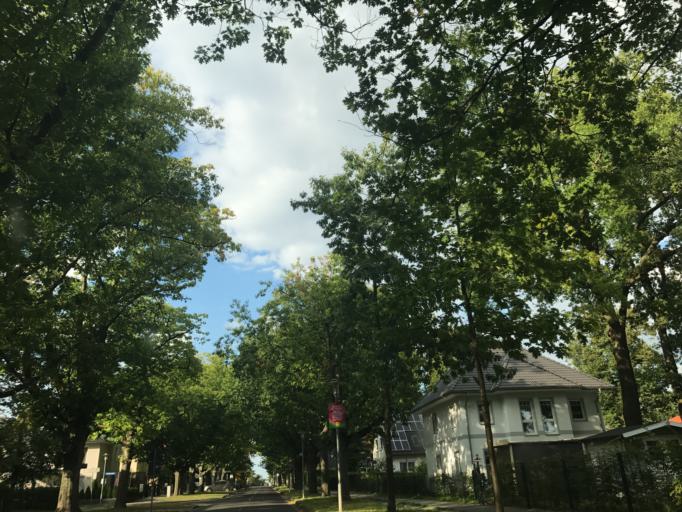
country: DE
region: Brandenburg
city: Dallgow-Doeberitz
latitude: 52.5388
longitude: 13.0548
